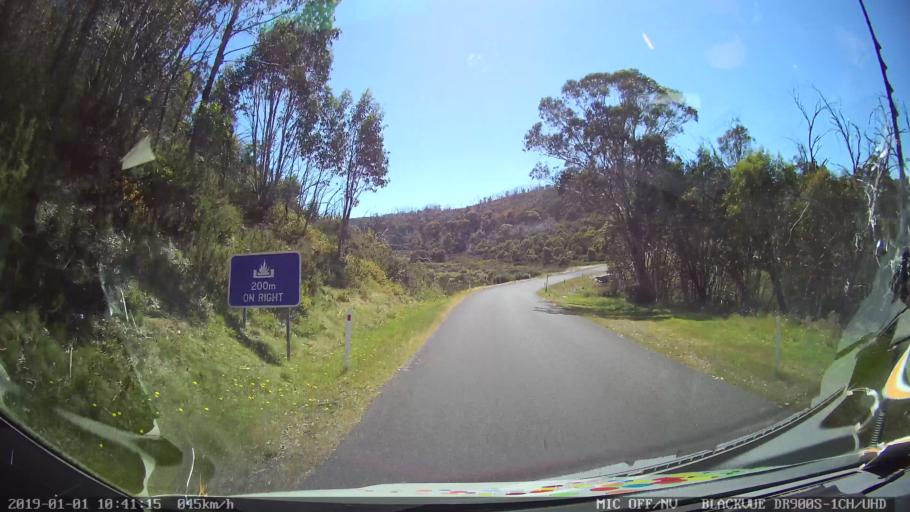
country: AU
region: New South Wales
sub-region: Snowy River
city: Jindabyne
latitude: -36.0368
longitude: 148.3187
